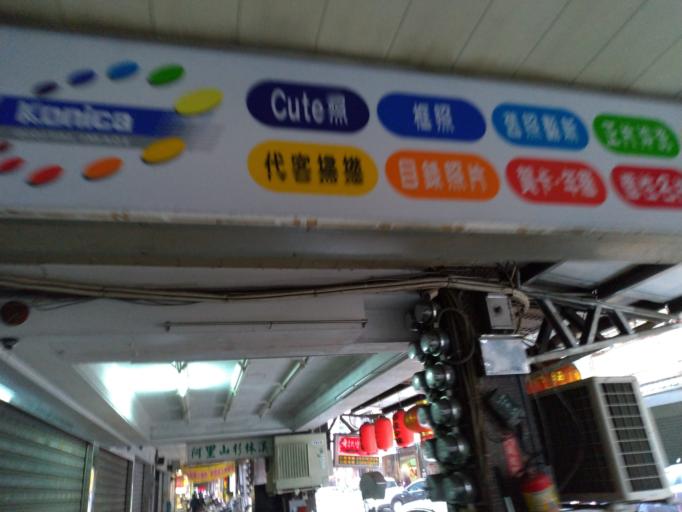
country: TW
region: Taiwan
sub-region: Keelung
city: Keelung
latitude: 25.0833
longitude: 121.6961
